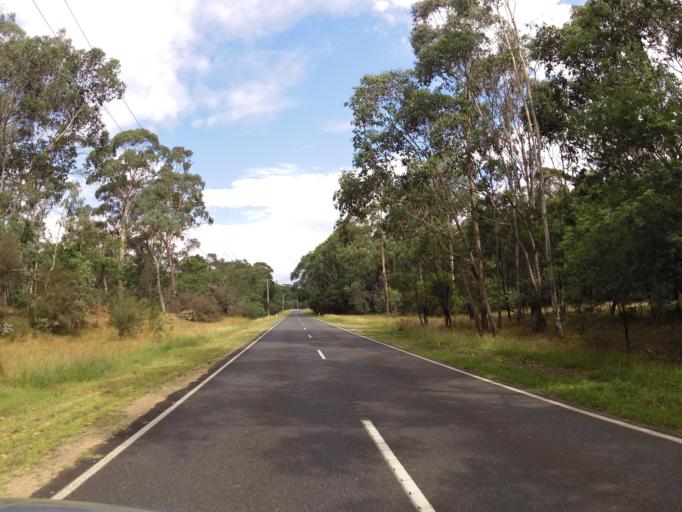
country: AU
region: Victoria
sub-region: Alpine
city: Mount Beauty
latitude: -36.7548
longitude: 147.0197
